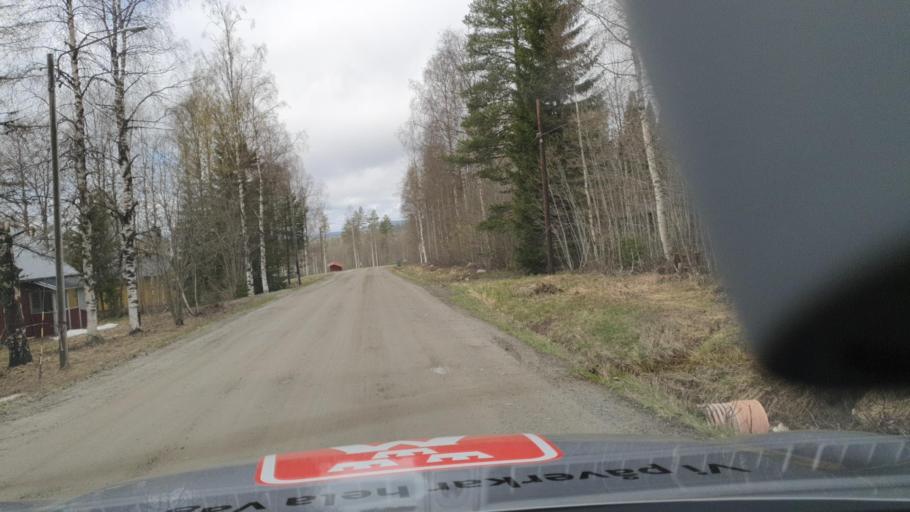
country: SE
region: Vaesterbotten
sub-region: Bjurholms Kommun
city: Bjurholm
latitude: 63.6851
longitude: 18.9686
